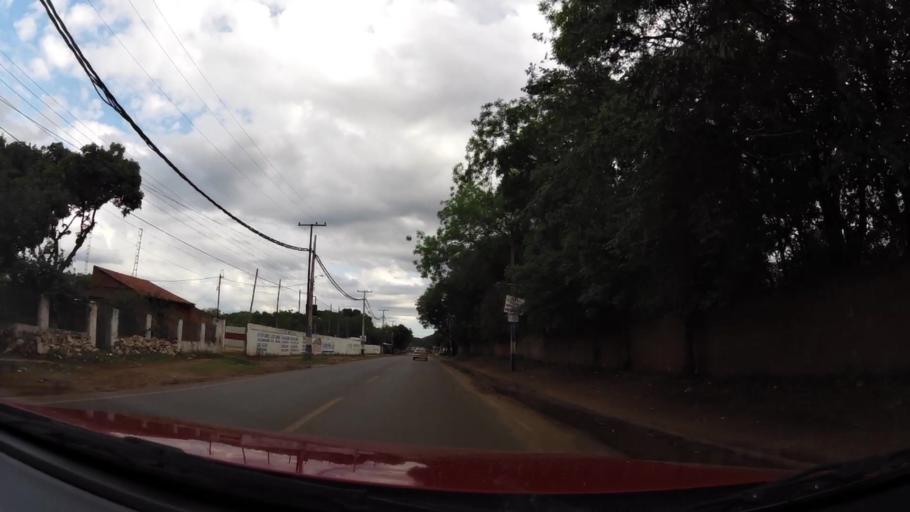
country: PY
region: Central
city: San Lorenzo
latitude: -25.2849
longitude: -57.4830
